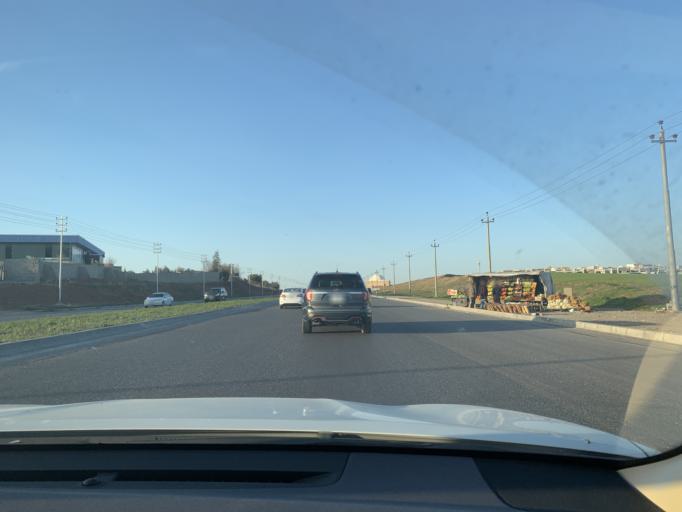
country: IQ
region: Arbil
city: Erbil
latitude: 36.2747
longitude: 44.0154
